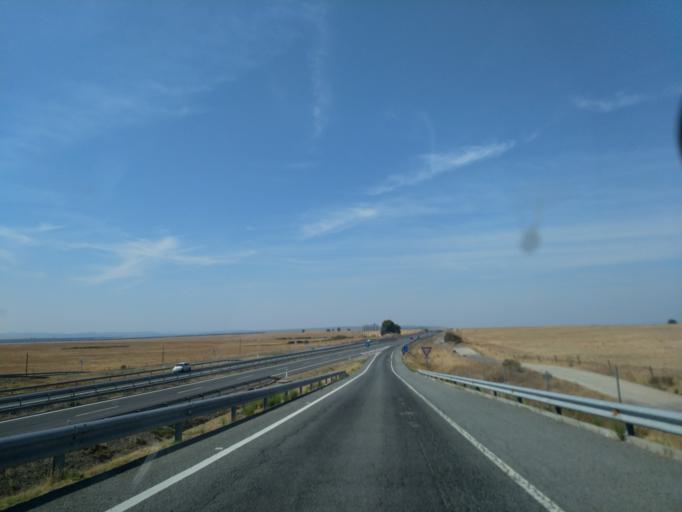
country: ES
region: Extremadura
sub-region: Provincia de Caceres
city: Berrocalejo
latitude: 39.8952
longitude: -5.3464
